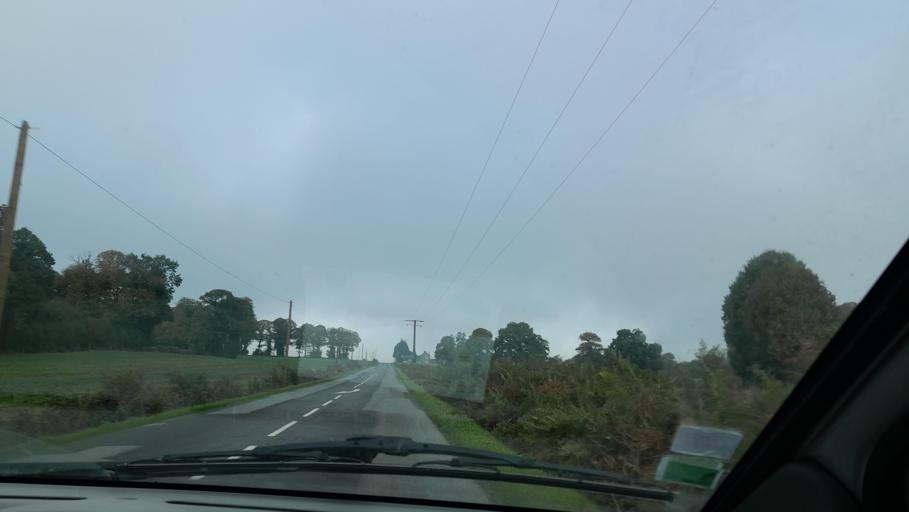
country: FR
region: Brittany
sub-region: Departement d'Ille-et-Vilaine
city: Luitre
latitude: 48.2452
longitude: -1.1181
